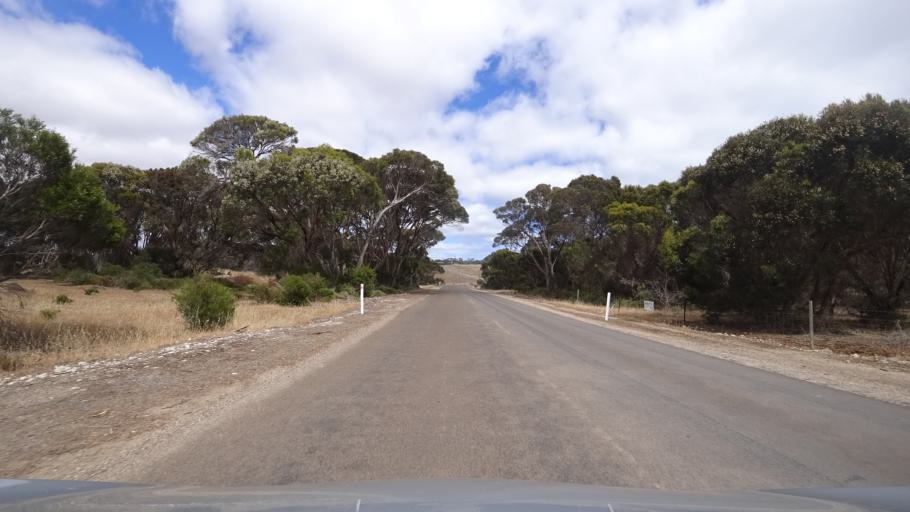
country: AU
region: South Australia
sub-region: Kangaroo Island
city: Kingscote
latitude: -35.5977
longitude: 137.5080
